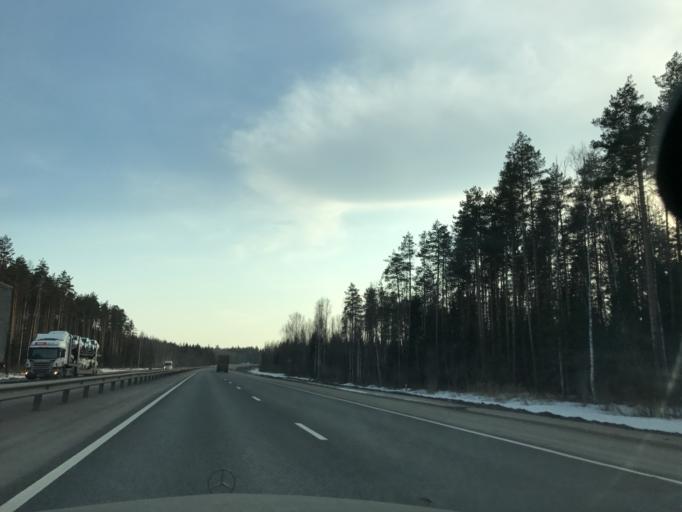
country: RU
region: Vladimir
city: Kameshkovo
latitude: 56.1813
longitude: 40.9474
